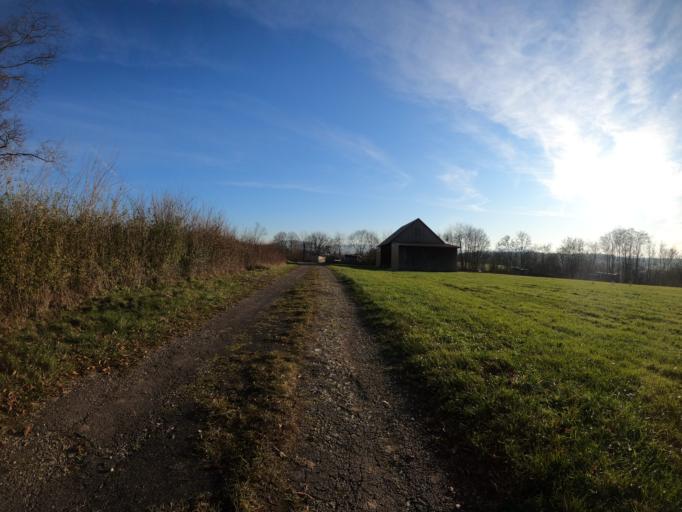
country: DE
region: Baden-Wuerttemberg
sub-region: Regierungsbezirk Stuttgart
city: Wangen
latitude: 48.7000
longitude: 9.6206
